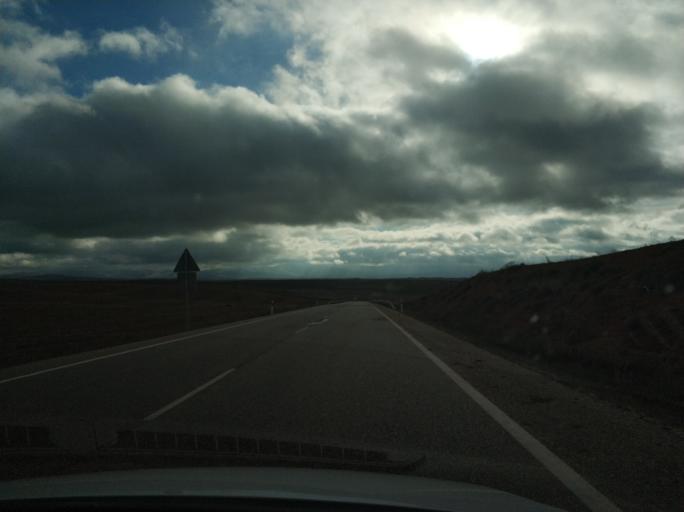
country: ES
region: Castille and Leon
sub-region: Provincia de Segovia
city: Ayllon
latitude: 41.4425
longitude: -3.3428
